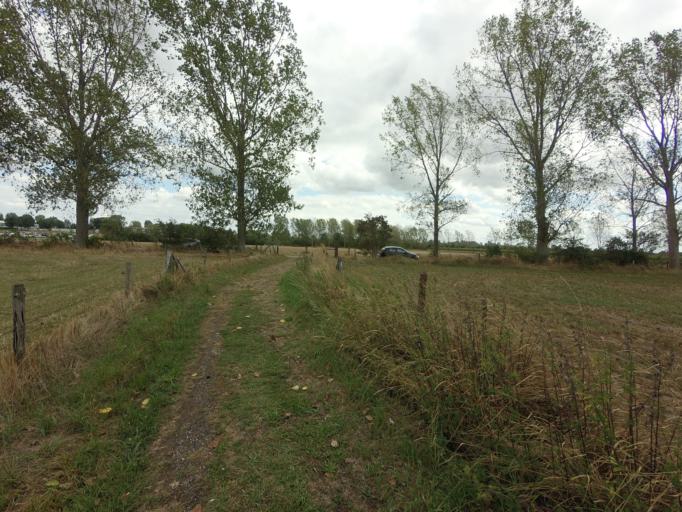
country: NL
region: Limburg
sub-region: Gemeente Maasgouw
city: Maasbracht
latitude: 51.1393
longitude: 5.8656
